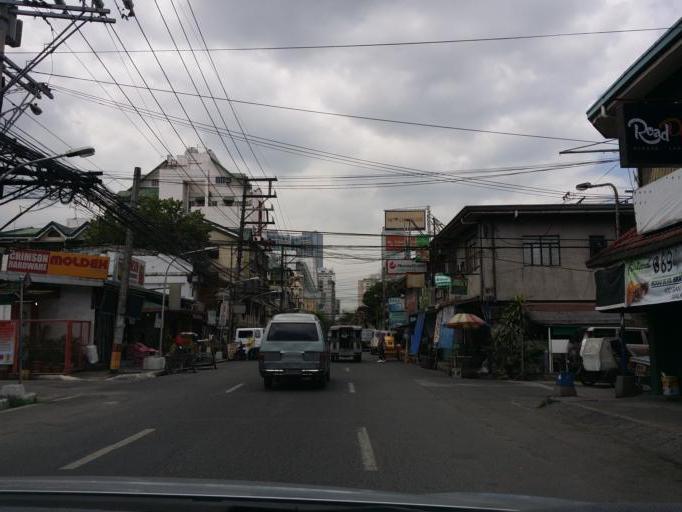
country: PH
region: Metro Manila
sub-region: Makati City
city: Makati City
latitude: 14.5655
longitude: 121.0011
